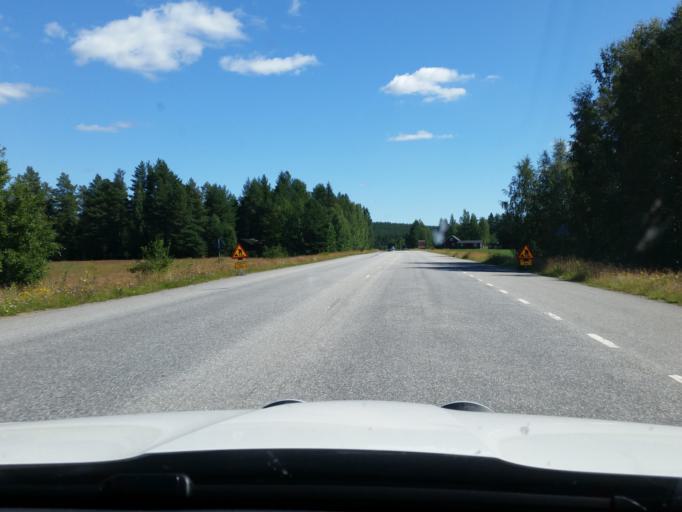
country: SE
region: Norrbotten
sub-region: Pitea Kommun
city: Bergsviken
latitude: 65.3149
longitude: 21.3205
